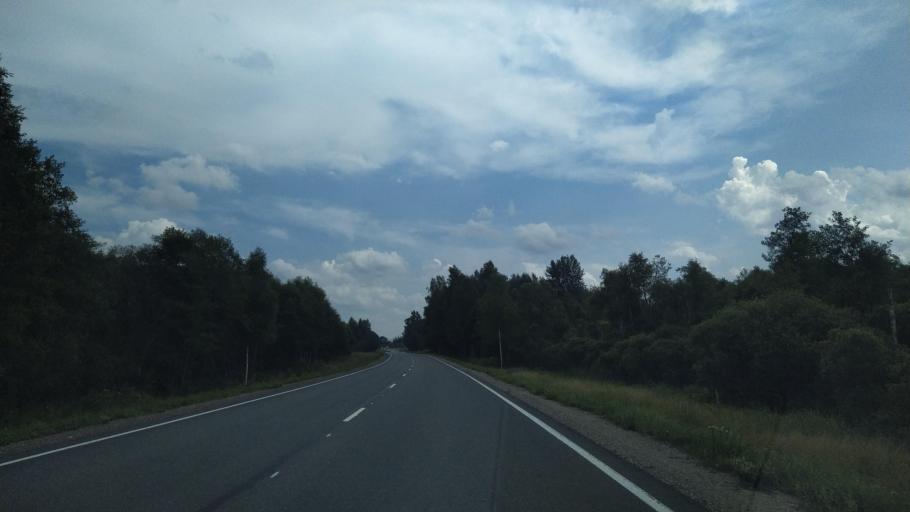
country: RU
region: Pskov
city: Pskov
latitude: 57.8186
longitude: 28.6540
